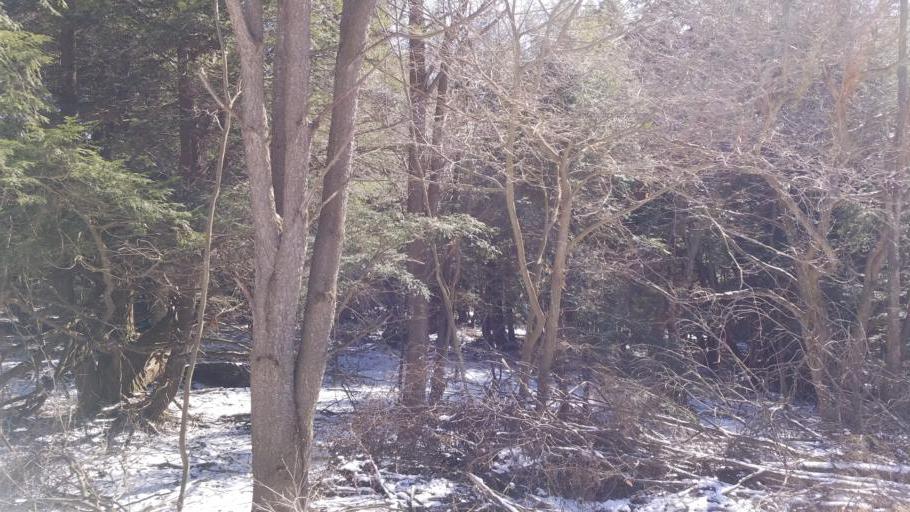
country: US
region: New York
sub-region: Allegany County
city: Andover
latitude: 41.9540
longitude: -77.7519
